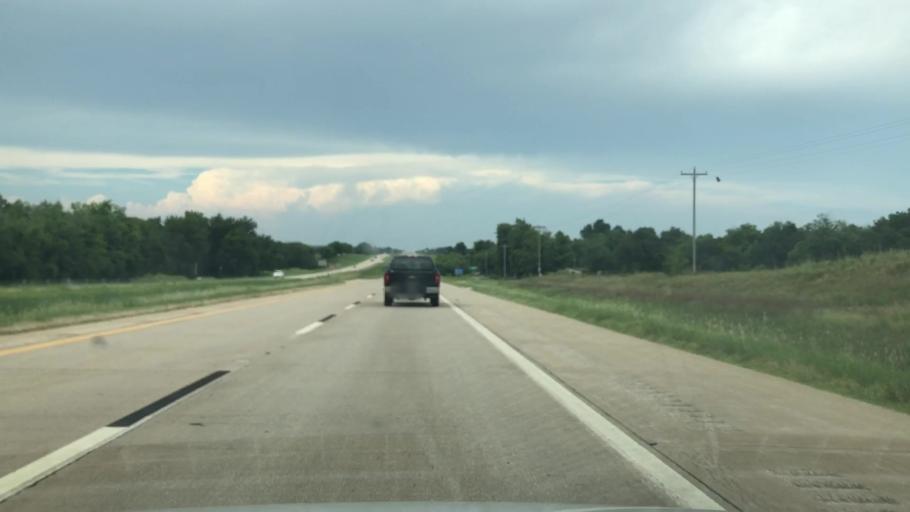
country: US
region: Oklahoma
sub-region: Osage County
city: Skiatook
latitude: 36.4367
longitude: -95.9203
